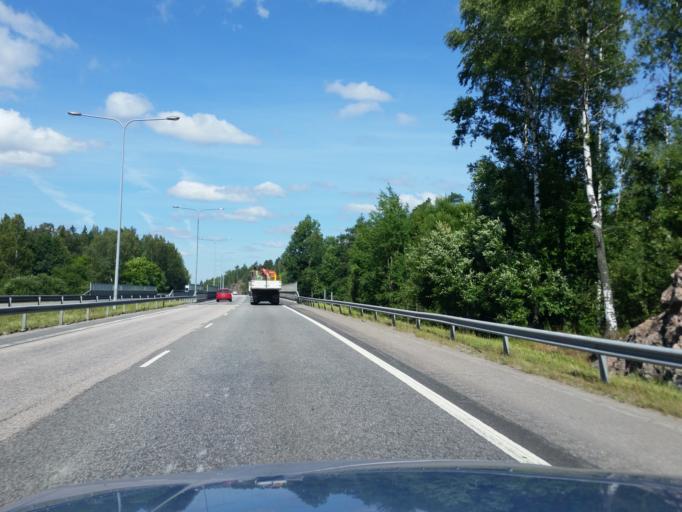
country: FI
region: Uusimaa
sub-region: Helsinki
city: Kauniainen
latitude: 60.2064
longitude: 24.6942
